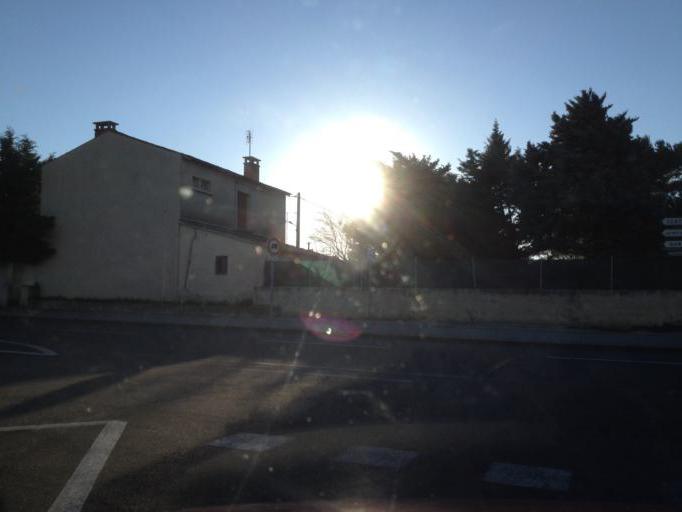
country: FR
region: Provence-Alpes-Cote d'Azur
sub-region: Departement du Vaucluse
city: Orange
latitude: 44.1449
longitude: 4.8113
